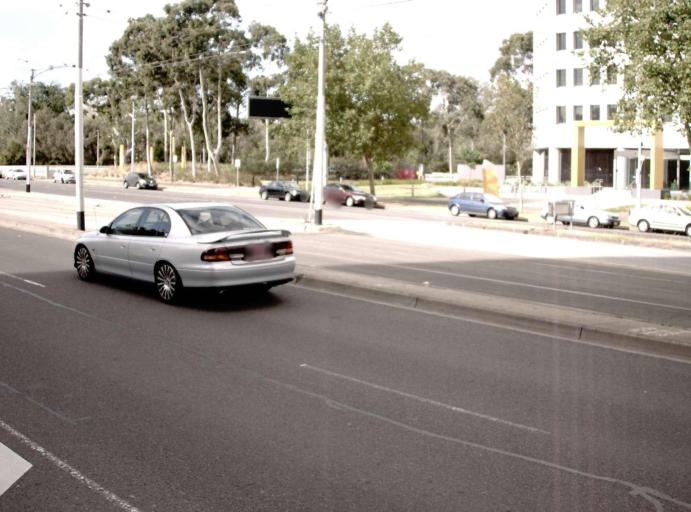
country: AU
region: Victoria
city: Windsor
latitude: -37.8542
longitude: 144.9823
